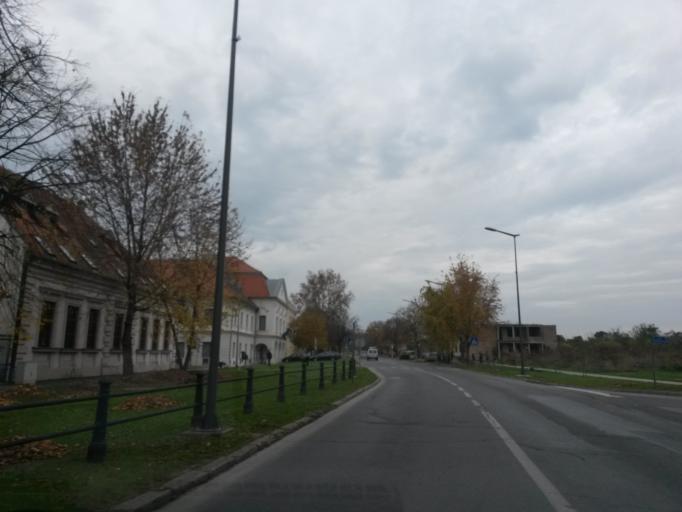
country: HR
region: Vukovarsko-Srijemska
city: Vukovar
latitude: 45.3552
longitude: 18.9993
